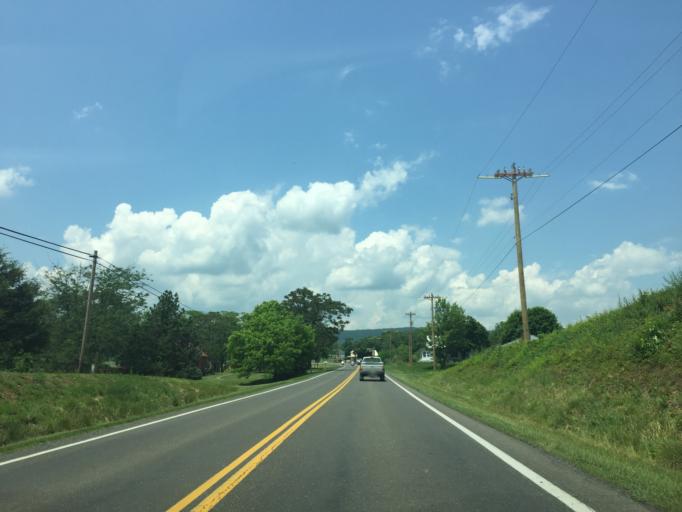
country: US
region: Virginia
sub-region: Shenandoah County
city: Strasburg
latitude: 39.0301
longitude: -78.3695
